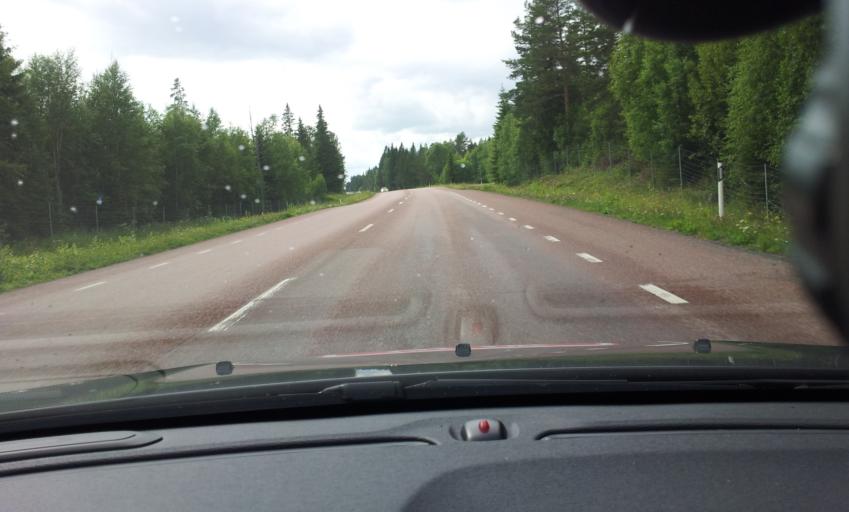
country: SE
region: Jaemtland
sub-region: Krokoms Kommun
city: Krokom
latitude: 63.3265
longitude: 14.3637
